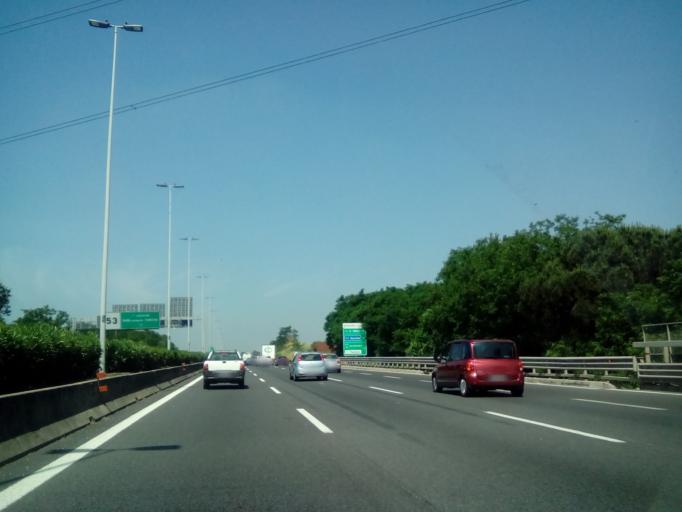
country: IT
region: Latium
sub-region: Citta metropolitana di Roma Capitale
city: Selcetta
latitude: 41.7982
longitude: 12.4759
